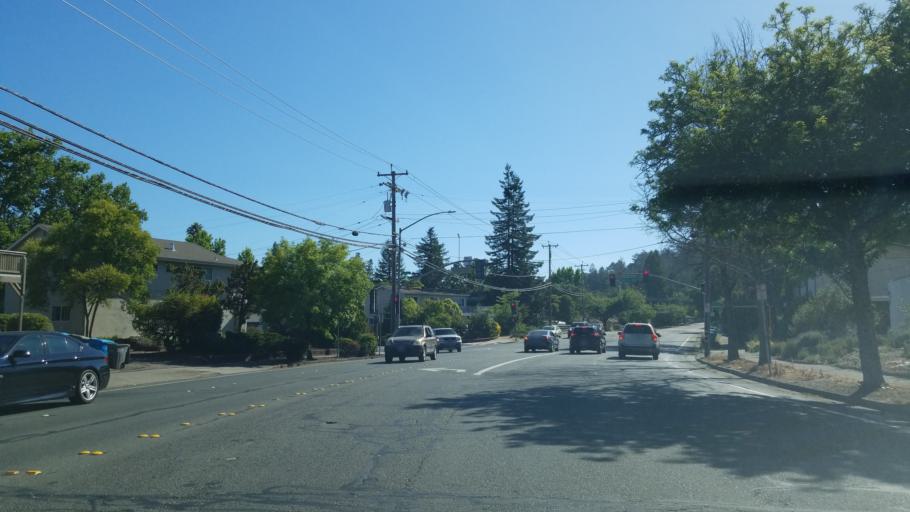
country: US
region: California
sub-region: Sonoma County
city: Santa Rosa
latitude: 38.4723
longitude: -122.6764
